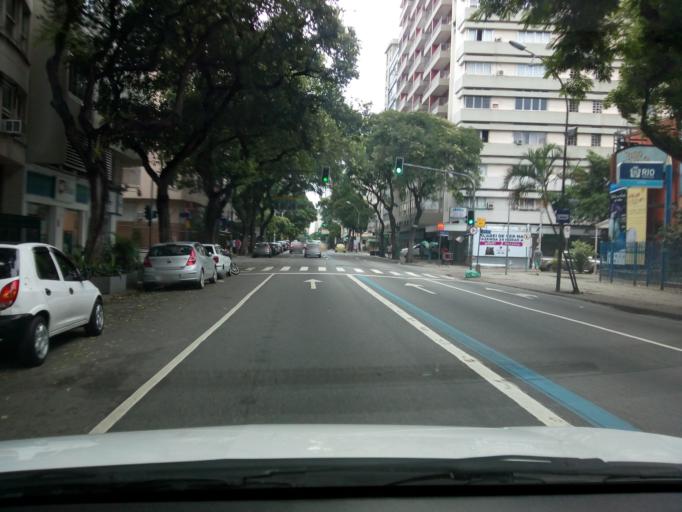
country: BR
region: Rio de Janeiro
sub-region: Rio De Janeiro
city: Rio de Janeiro
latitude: -22.9652
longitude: -43.1805
